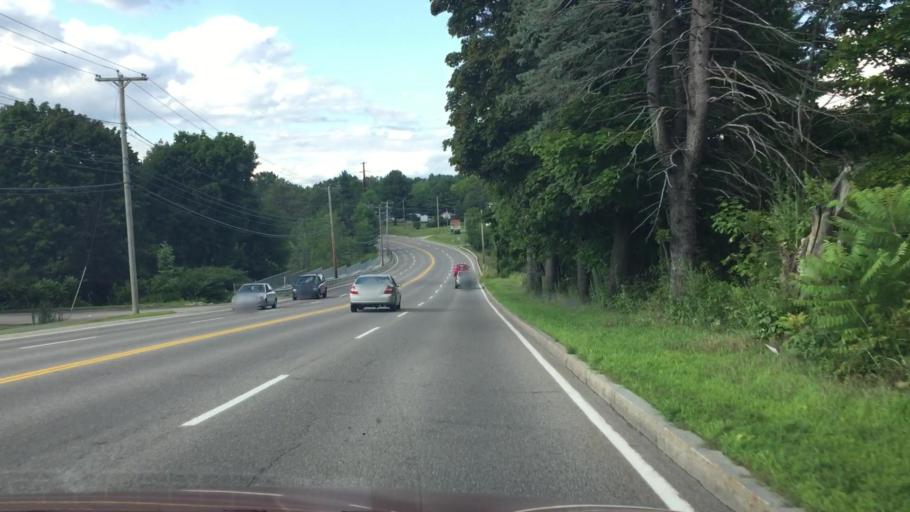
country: US
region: Maine
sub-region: York County
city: Saco
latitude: 43.5167
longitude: -70.4286
